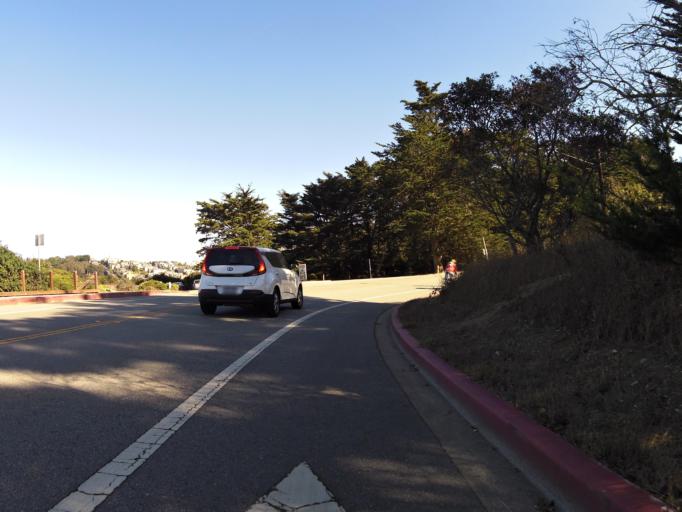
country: US
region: California
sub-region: San Francisco County
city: San Francisco
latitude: 37.7920
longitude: -122.4590
